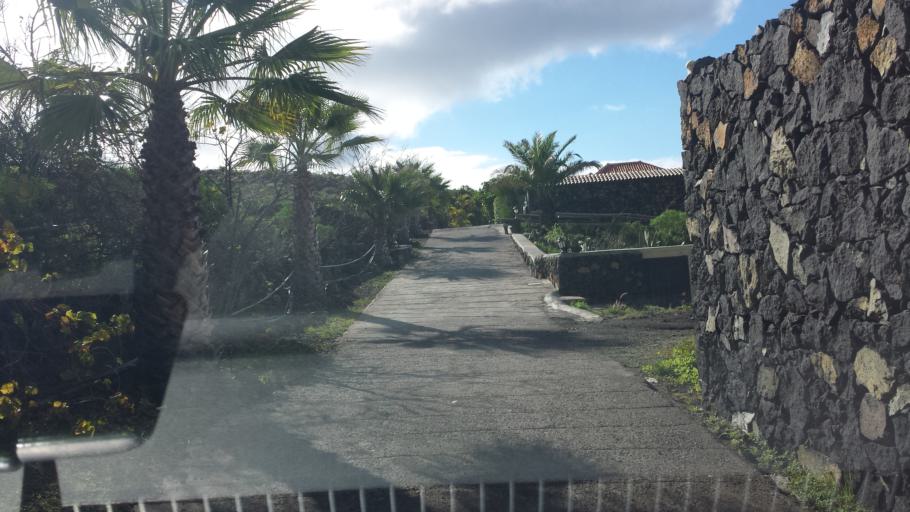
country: ES
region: Canary Islands
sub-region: Provincia de Santa Cruz de Tenerife
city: El Paso
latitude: 28.6098
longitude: -17.8907
